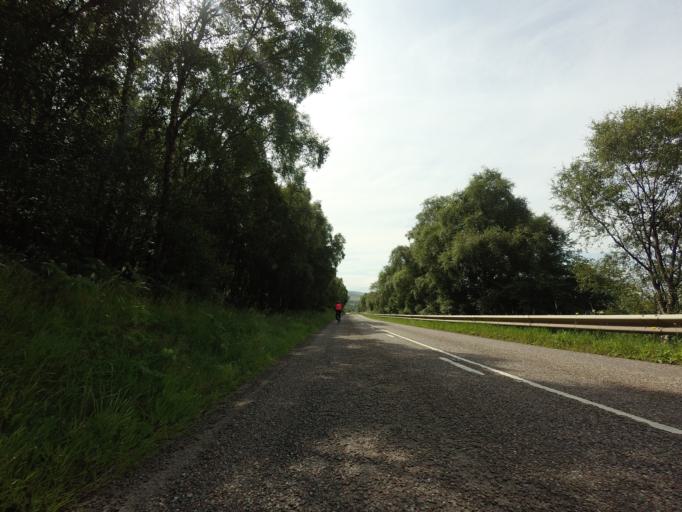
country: GB
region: Scotland
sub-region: Highland
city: Alness
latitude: 57.8547
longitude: -4.2561
